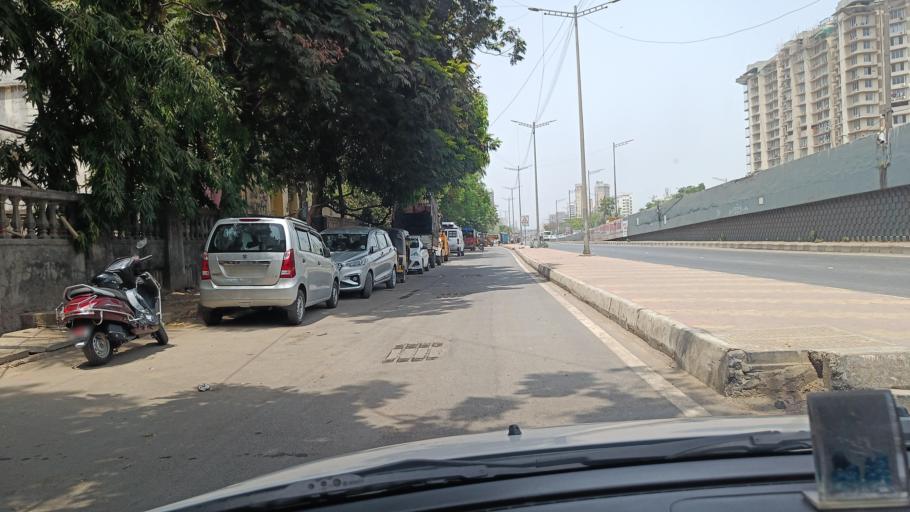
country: IN
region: Maharashtra
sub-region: Mumbai Suburban
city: Mumbai
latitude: 19.0582
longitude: 72.8888
